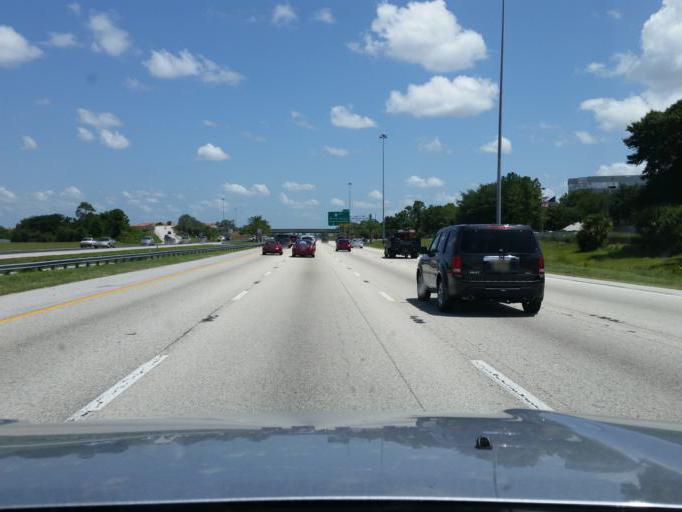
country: US
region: Florida
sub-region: Orange County
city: Williamsburg
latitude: 28.4145
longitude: -81.4741
